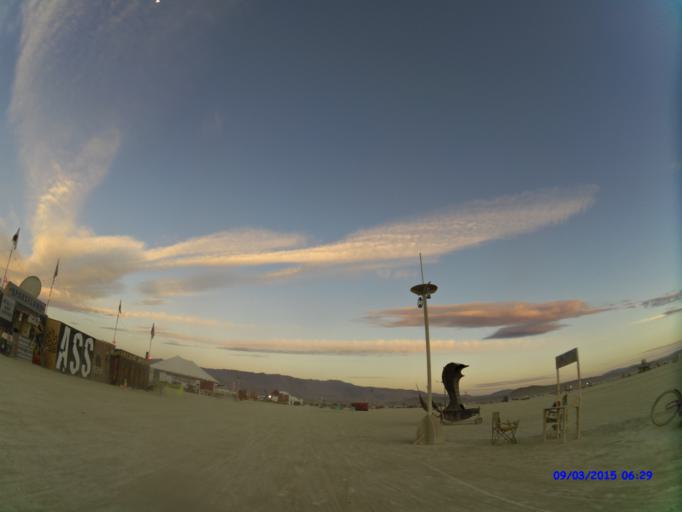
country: US
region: Nevada
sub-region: Pershing County
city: Lovelock
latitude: 40.7796
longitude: -119.2076
